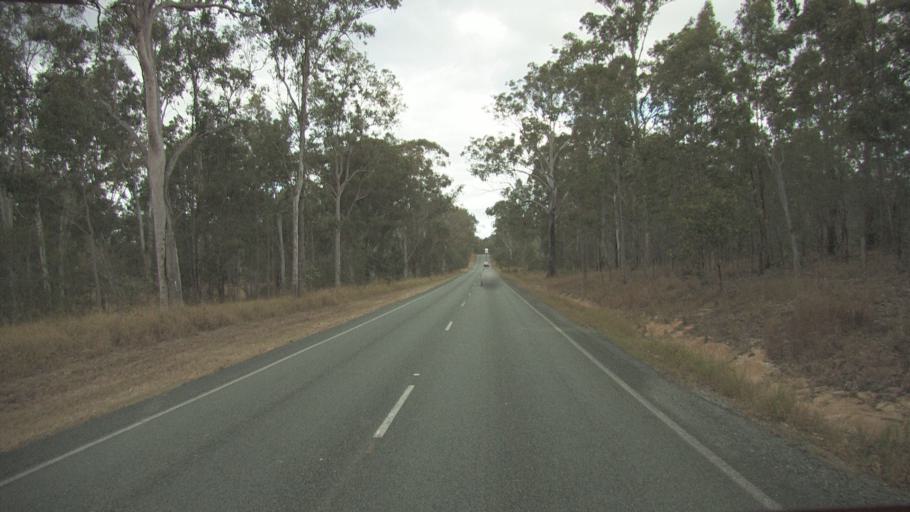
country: AU
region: Queensland
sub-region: Logan
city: Cedar Vale
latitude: -27.9034
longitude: 153.0906
